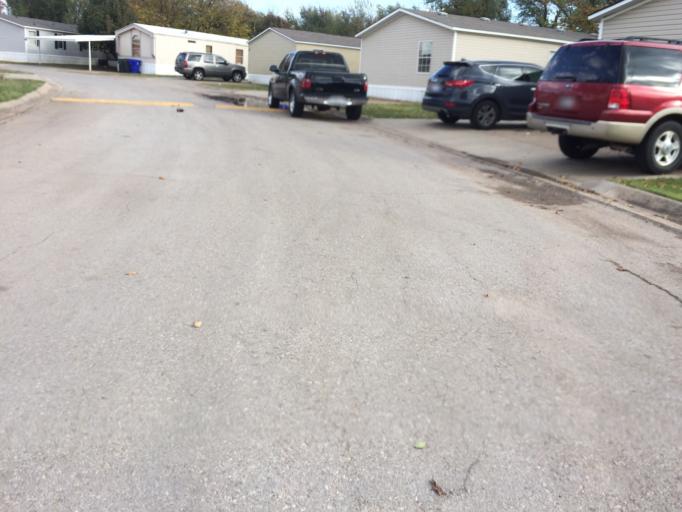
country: US
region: Oklahoma
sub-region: Cleveland County
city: Norman
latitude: 35.2381
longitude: -97.4539
